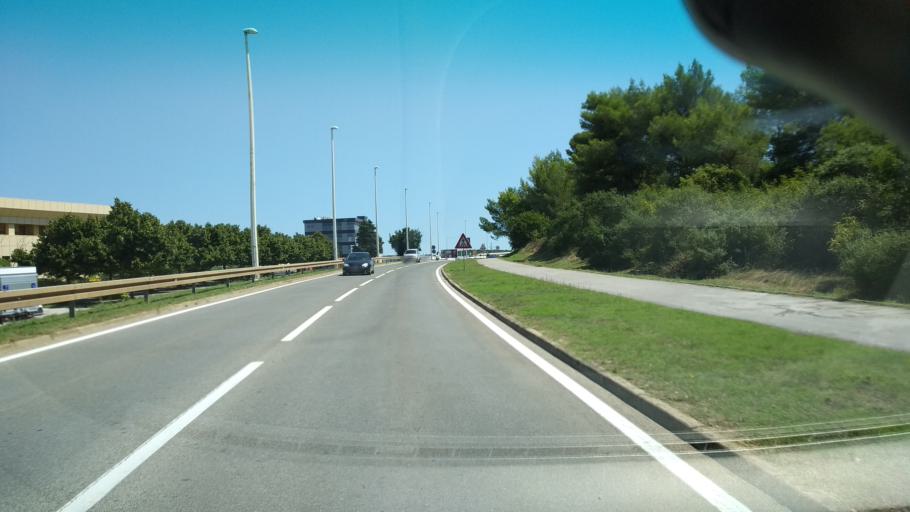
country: HR
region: Istarska
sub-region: Grad Pula
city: Pula
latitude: 44.8859
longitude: 13.8542
